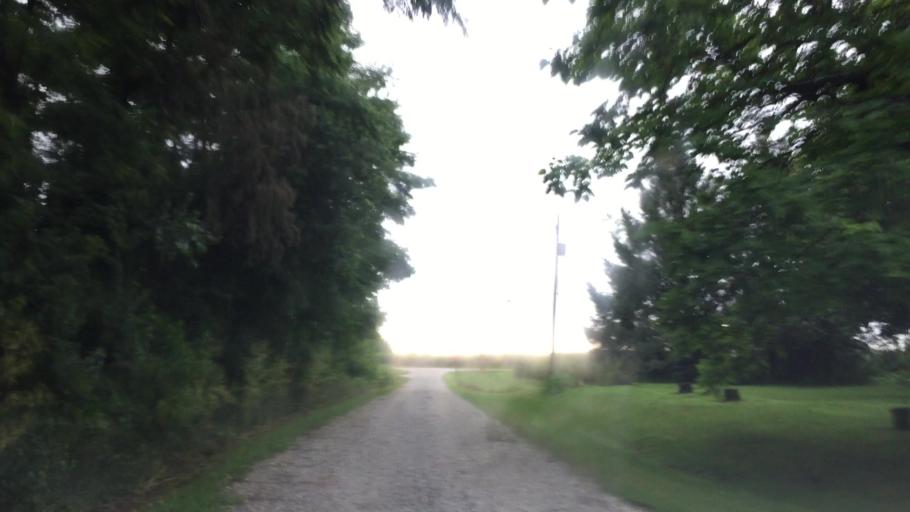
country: US
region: Illinois
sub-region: Hancock County
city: Nauvoo
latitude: 40.5510
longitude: -91.3512
